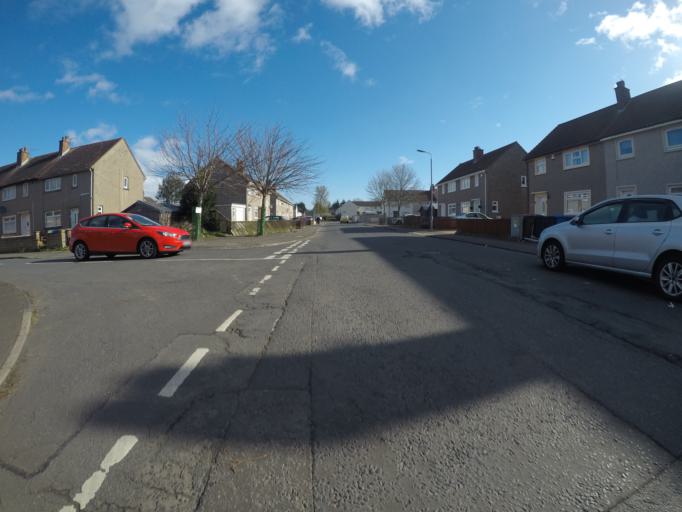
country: GB
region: Scotland
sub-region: North Ayrshire
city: Irvine
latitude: 55.6256
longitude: -4.6581
